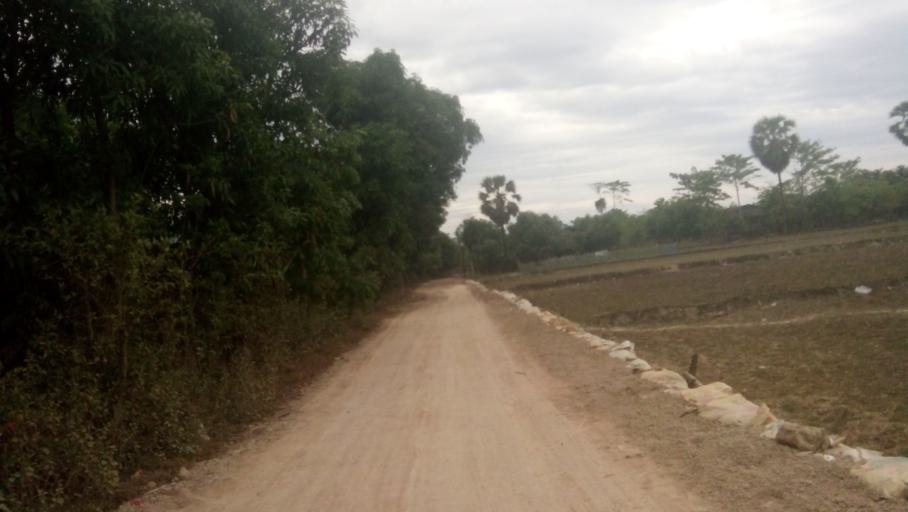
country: MM
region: Kayin
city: Hpa-an
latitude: 17.1164
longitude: 97.8185
